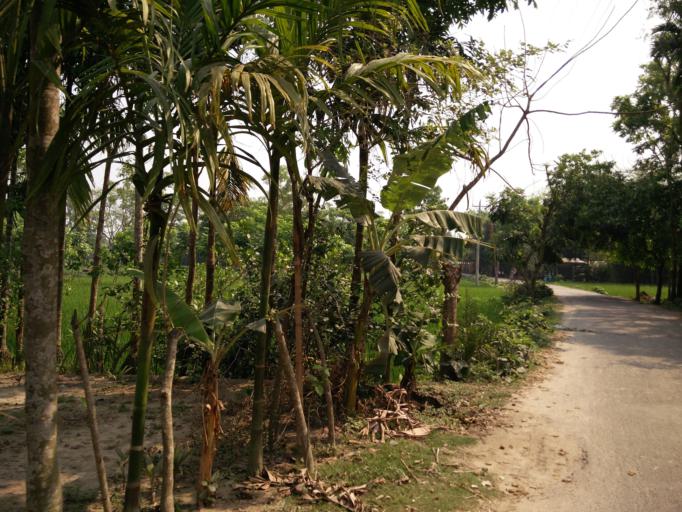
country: BD
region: Dhaka
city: Muktagacha
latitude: 24.9270
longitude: 90.2485
